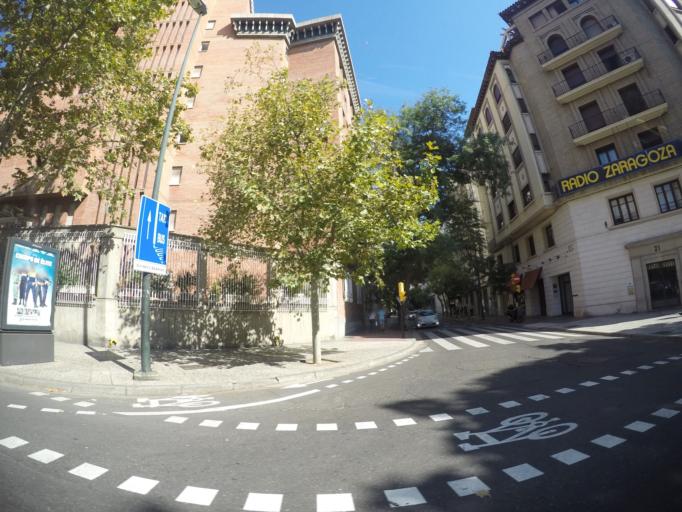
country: ES
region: Aragon
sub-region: Provincia de Zaragoza
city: Zaragoza
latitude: 41.6484
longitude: -0.8818
